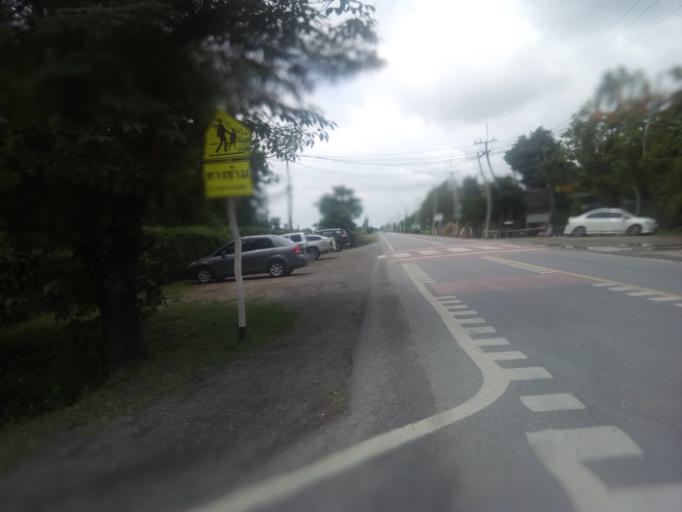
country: TH
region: Pathum Thani
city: Ban Lam Luk Ka
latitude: 14.0107
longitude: 100.8228
